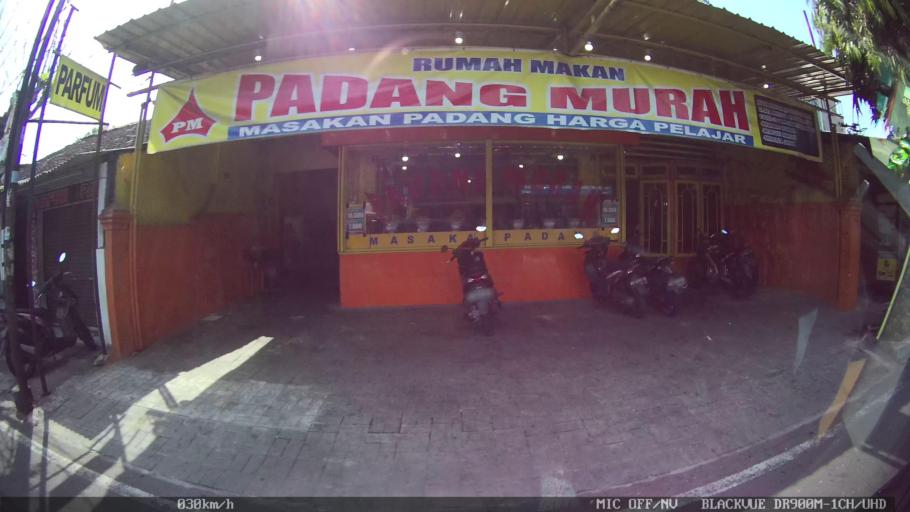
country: ID
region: Daerah Istimewa Yogyakarta
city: Yogyakarta
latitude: -7.8075
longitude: 110.3879
